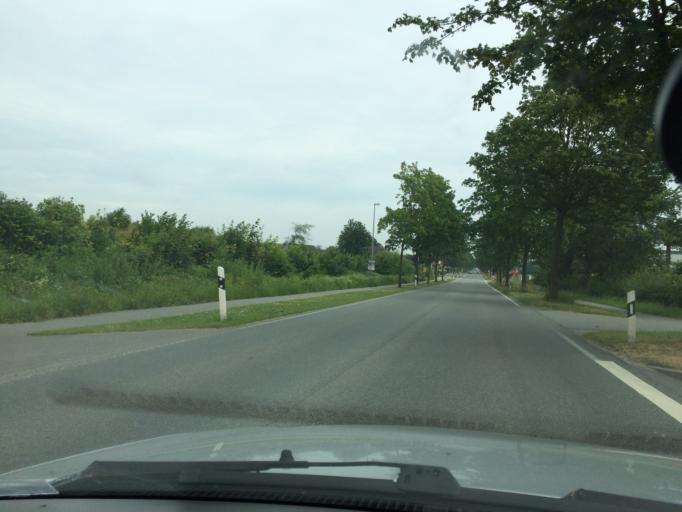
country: DE
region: Schleswig-Holstein
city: Jarplund-Weding
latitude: 54.7395
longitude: 9.4408
